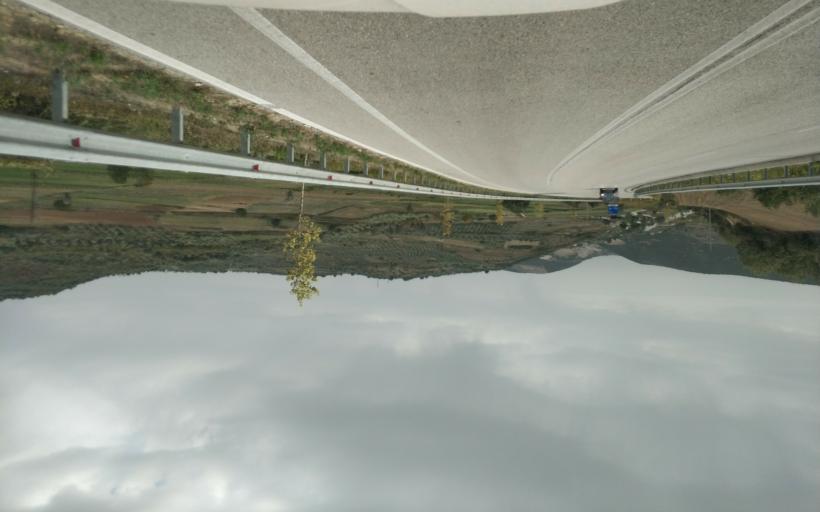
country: AL
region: Fier
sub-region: Rrethi i Mallakastres
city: Fratar
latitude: 40.4946
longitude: 19.8292
